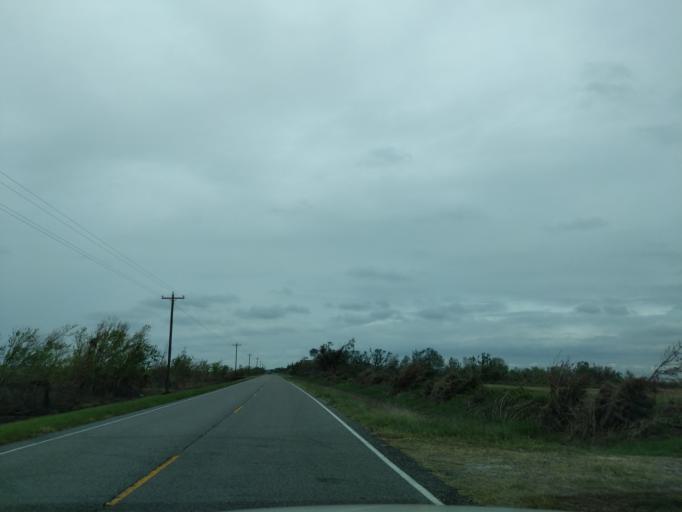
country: US
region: Louisiana
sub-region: Cameron Parish
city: Cameron
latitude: 29.7867
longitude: -93.1450
